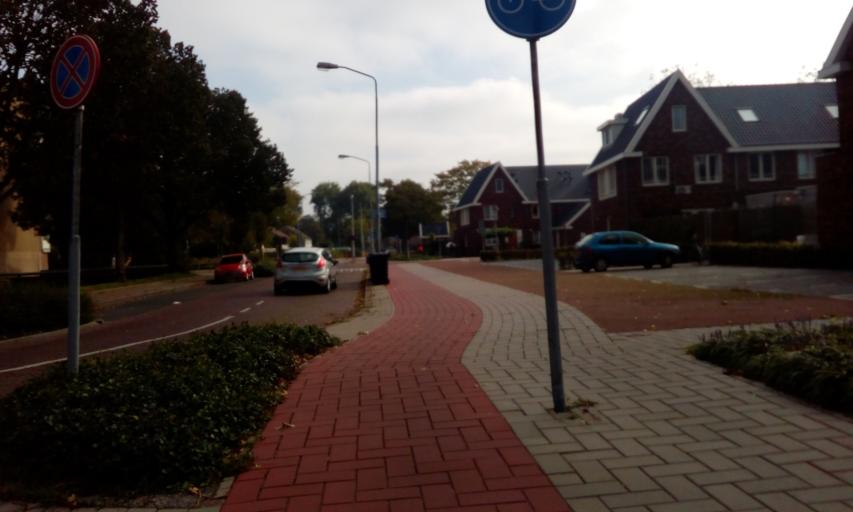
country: NL
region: South Holland
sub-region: Gemeente Voorschoten
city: Voorschoten
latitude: 52.1435
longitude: 4.4584
